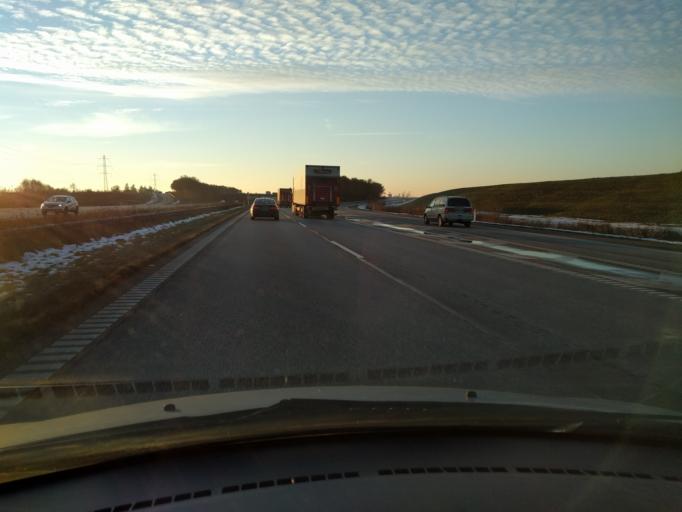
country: DK
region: Zealand
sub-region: Koge Kommune
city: Borup
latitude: 55.4580
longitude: 11.9891
